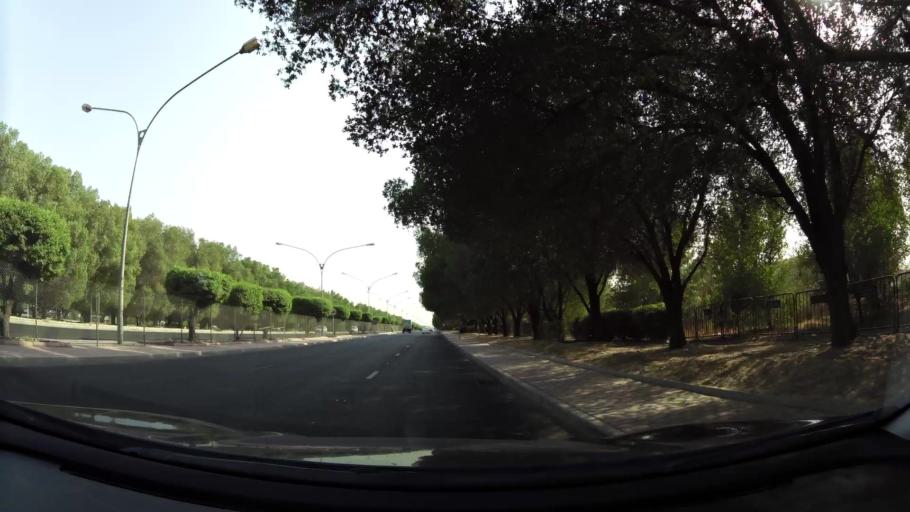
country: KW
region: Mubarak al Kabir
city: Sabah as Salim
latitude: 29.2788
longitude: 48.0628
